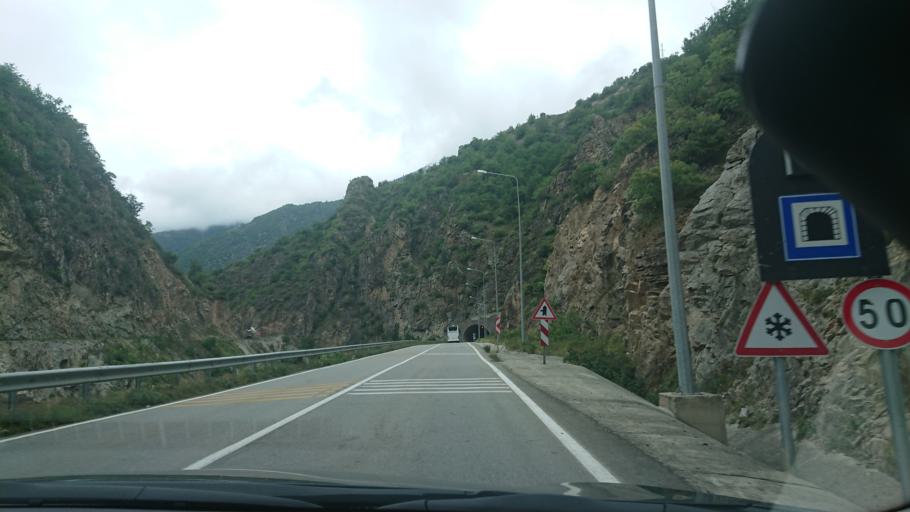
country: TR
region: Gumushane
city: Kurtun
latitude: 40.7060
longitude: 39.0658
